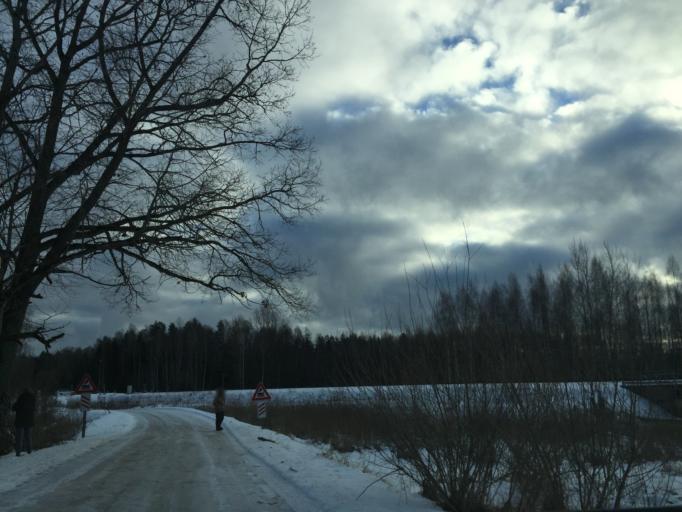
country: LV
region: Lielvarde
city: Lielvarde
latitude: 56.5751
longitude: 24.7980
